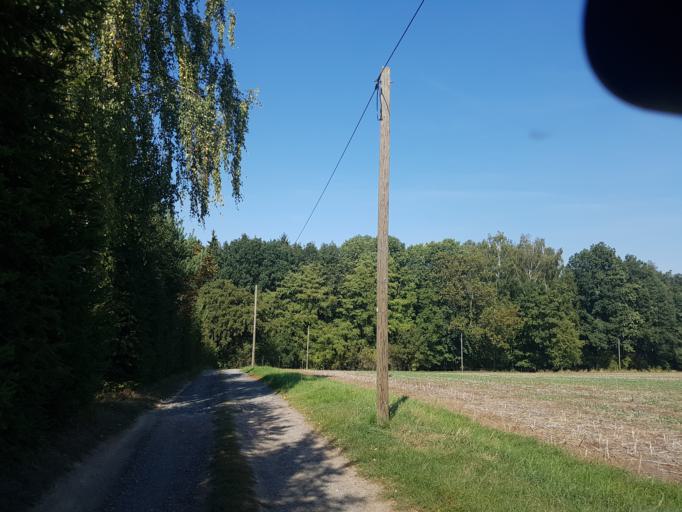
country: DE
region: Saxony
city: Kriebstein
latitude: 51.0461
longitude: 13.0068
